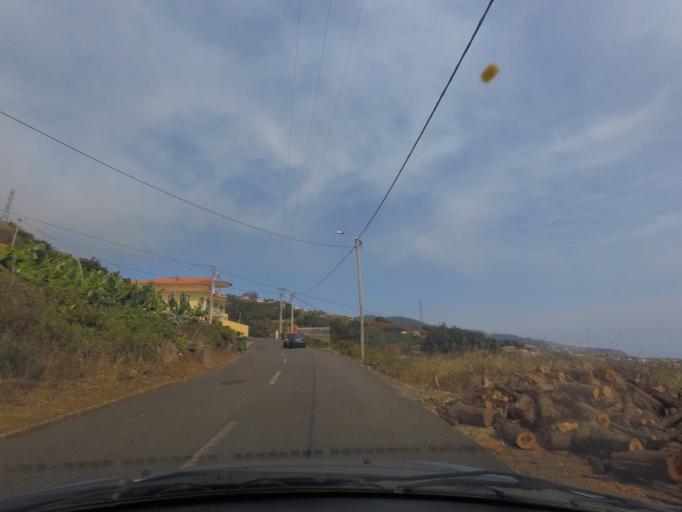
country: PT
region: Madeira
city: Ribeira Brava
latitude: 32.6868
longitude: -17.0666
